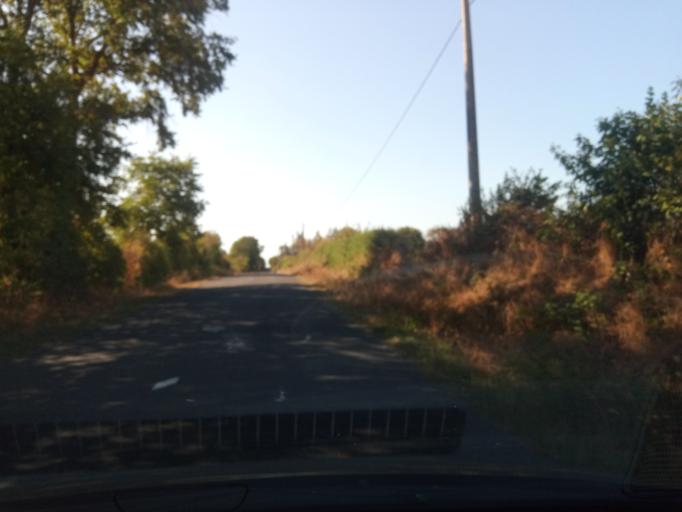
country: FR
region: Poitou-Charentes
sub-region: Departement de la Vienne
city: Saulge
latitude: 46.3698
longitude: 0.8828
